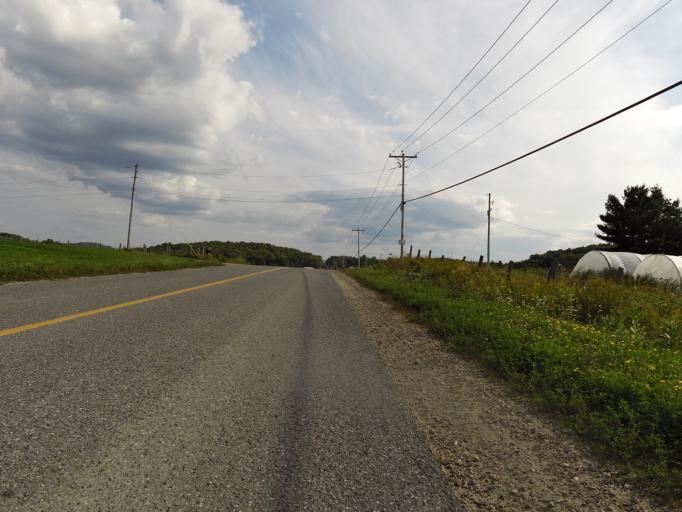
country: CA
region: Quebec
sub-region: Outaouais
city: Wakefield
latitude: 45.6601
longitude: -76.0177
